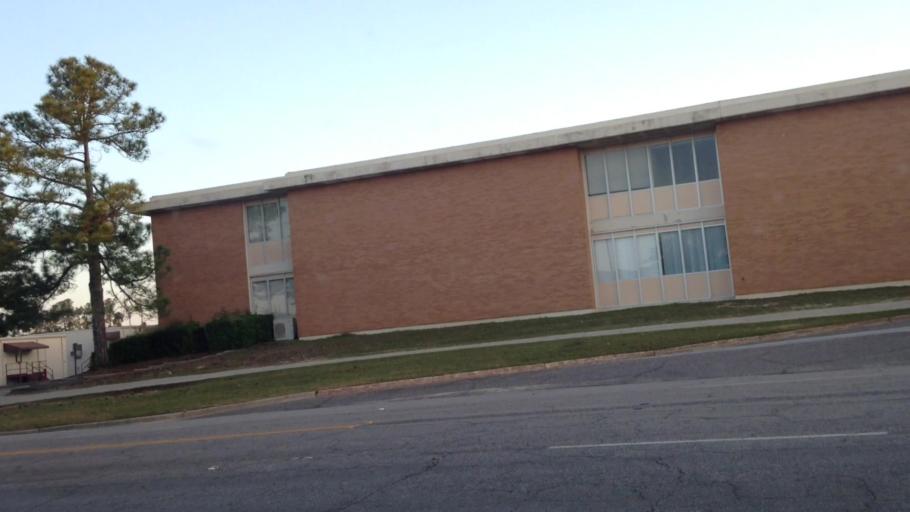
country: US
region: Georgia
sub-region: Columbia County
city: Grovetown
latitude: 33.4253
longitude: -82.1491
